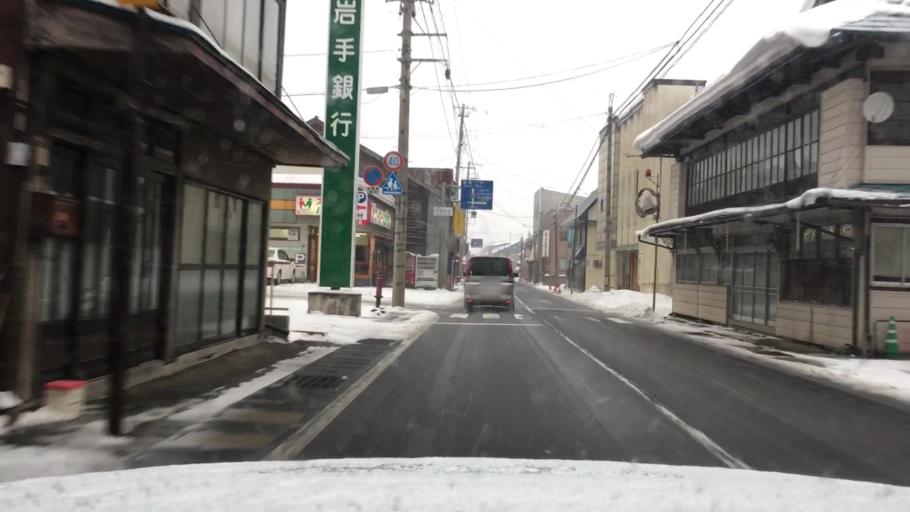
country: JP
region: Iwate
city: Ichinohe
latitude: 40.0984
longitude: 141.0478
